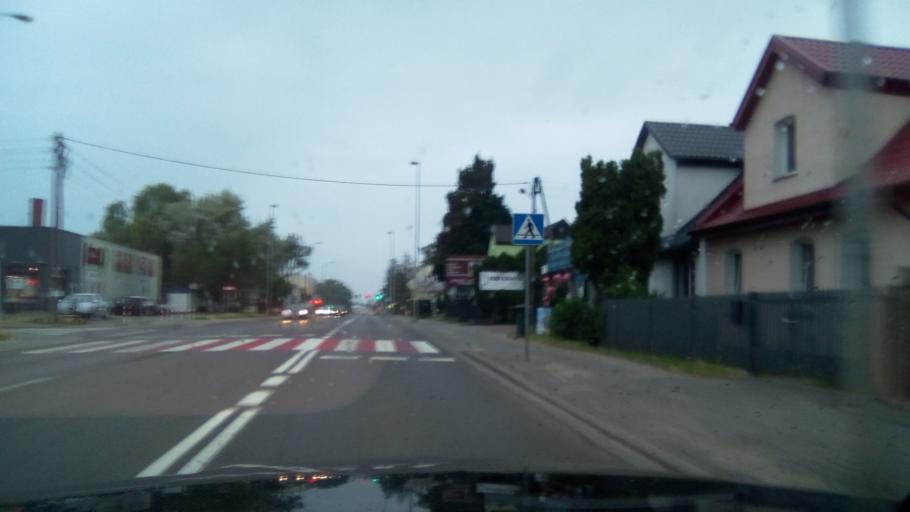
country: PL
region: Greater Poland Voivodeship
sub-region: Powiat poznanski
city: Swarzedz
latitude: 52.4105
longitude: 17.0847
